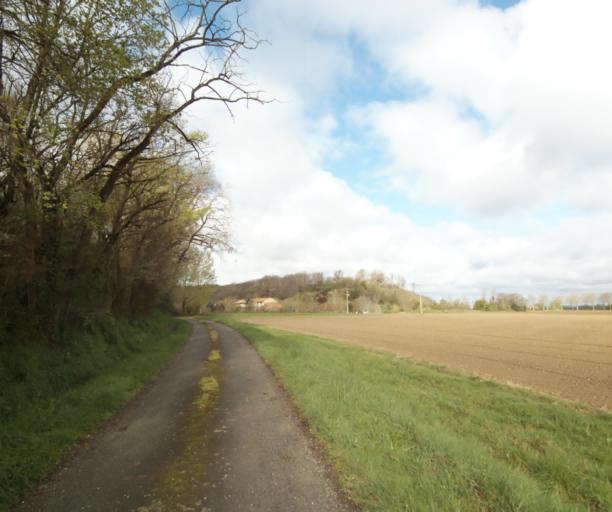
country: FR
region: Midi-Pyrenees
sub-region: Departement de l'Ariege
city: Saverdun
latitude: 43.2459
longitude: 1.5485
